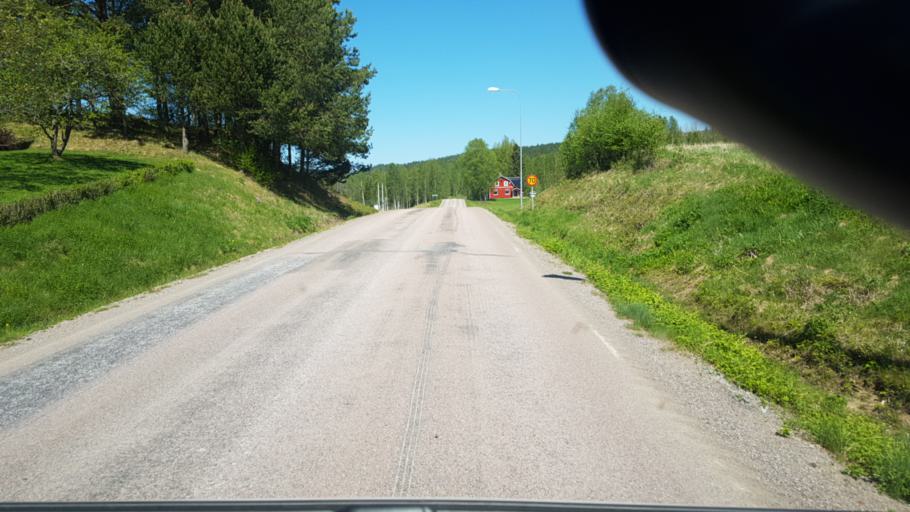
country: SE
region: Vaermland
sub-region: Eda Kommun
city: Amotfors
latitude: 59.8866
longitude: 12.5237
